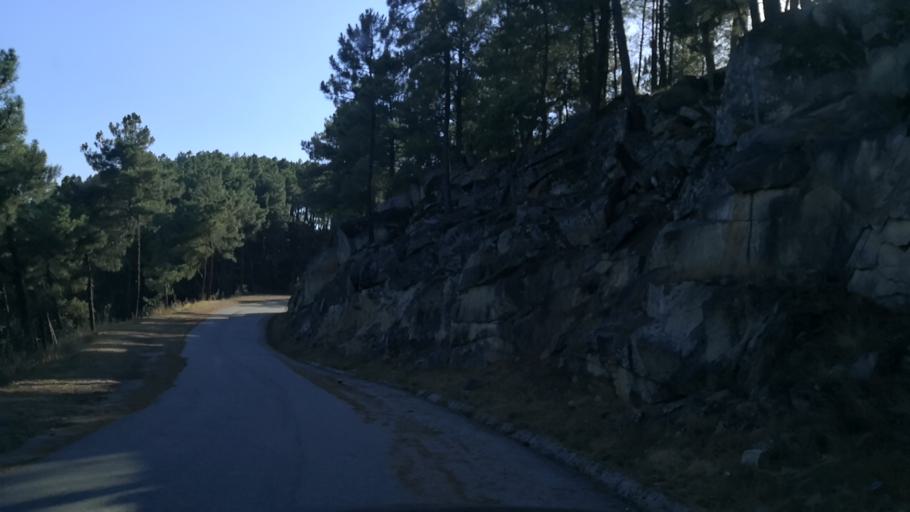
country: PT
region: Viseu
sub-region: Sao Joao da Pesqueira
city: Sao Joao da Pesqueira
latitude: 41.2548
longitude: -7.4189
